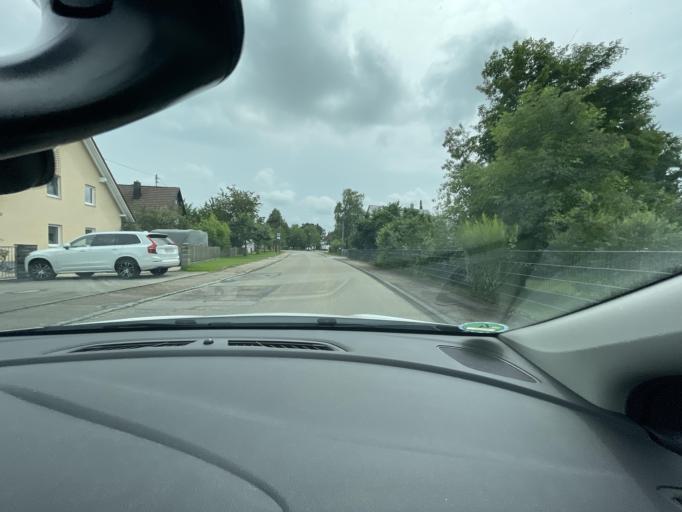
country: DE
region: Bavaria
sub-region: Swabia
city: Meitingen
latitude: 48.5618
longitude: 10.8607
